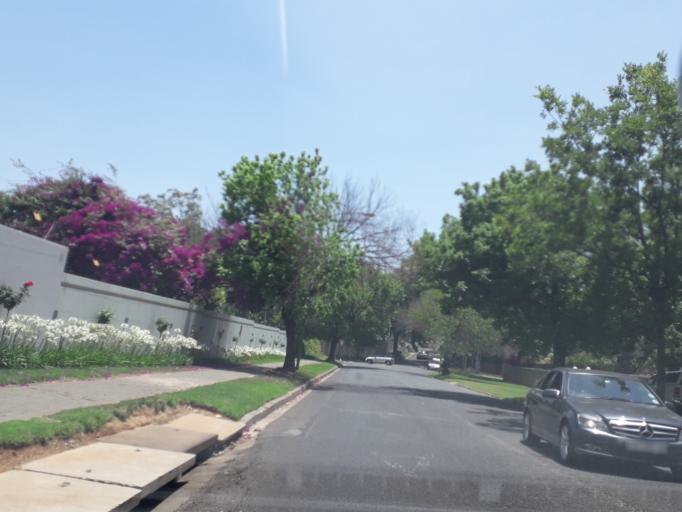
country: ZA
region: Gauteng
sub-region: City of Johannesburg Metropolitan Municipality
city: Johannesburg
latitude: -26.1334
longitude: 28.0297
